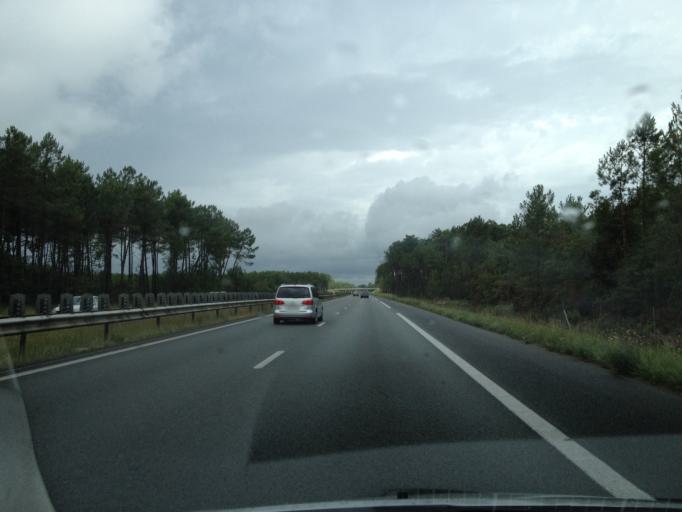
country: FR
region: Aquitaine
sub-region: Departement de la Gironde
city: Illats
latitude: 44.6281
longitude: -0.4042
